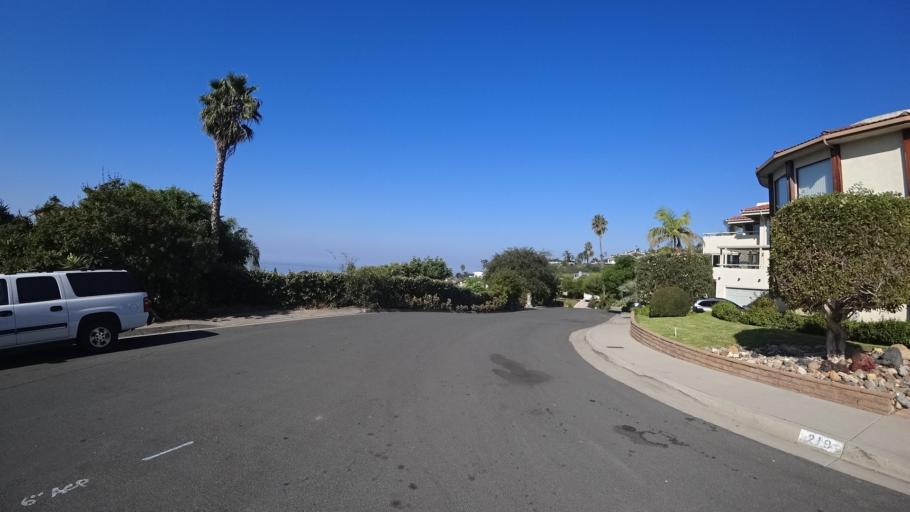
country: US
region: California
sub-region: Orange County
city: San Clemente
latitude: 33.4196
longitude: -117.5992
